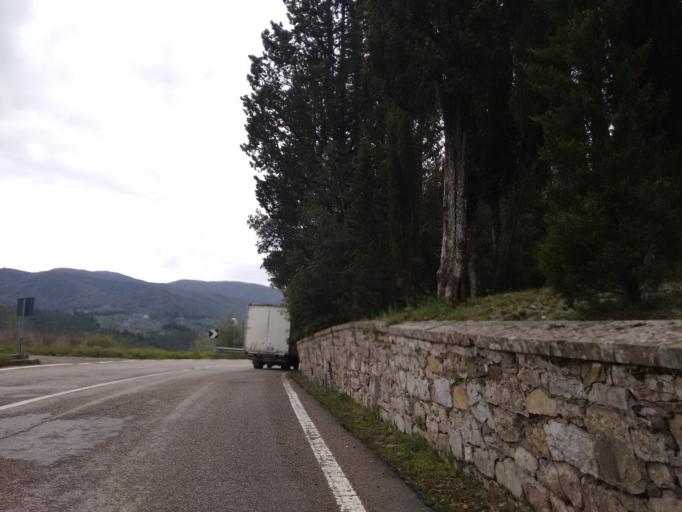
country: IT
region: Tuscany
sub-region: Province of Florence
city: Strada in Chianti
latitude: 43.6547
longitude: 11.3069
